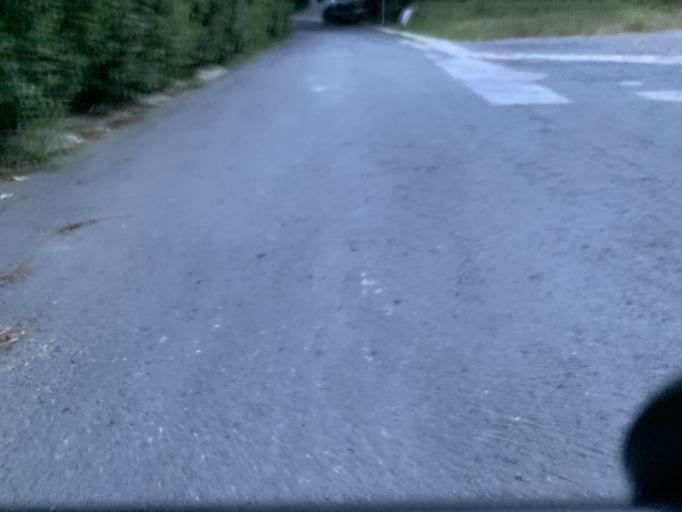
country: MX
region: Nuevo Leon
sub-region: Juarez
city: Bosques de San Pedro
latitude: 25.5171
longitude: -100.1834
